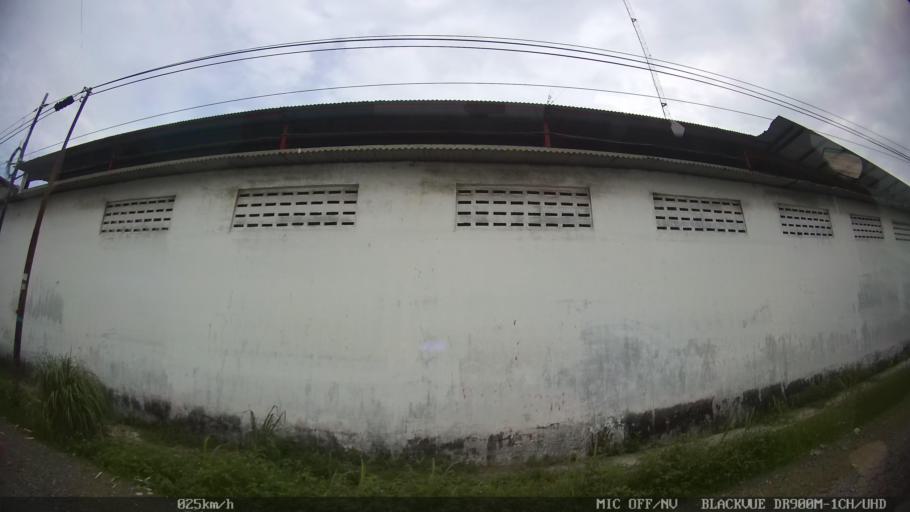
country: ID
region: North Sumatra
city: Sunggal
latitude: 3.6147
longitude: 98.5849
